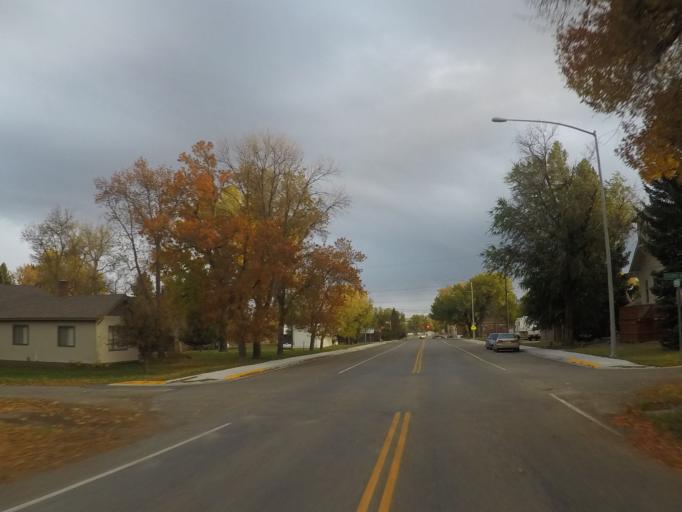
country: US
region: Montana
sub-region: Golden Valley County
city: Ryegate
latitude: 46.3002
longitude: -109.2562
